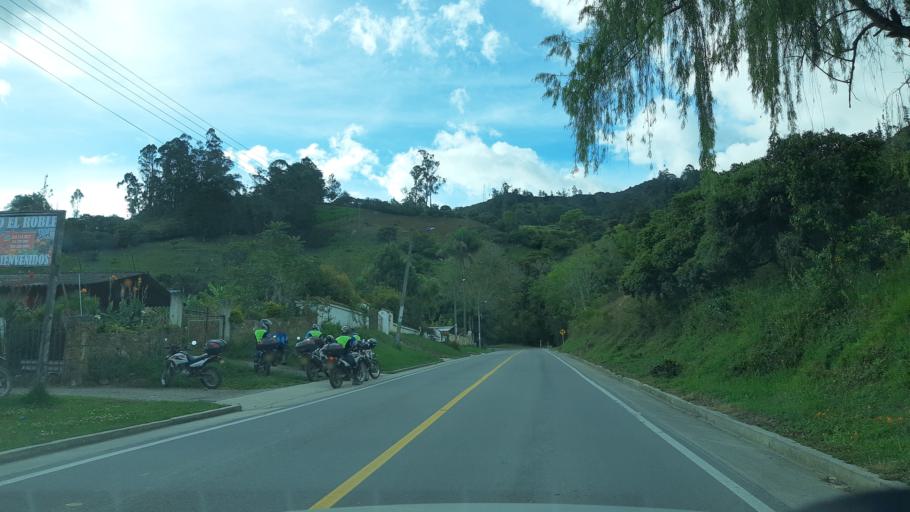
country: CO
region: Cundinamarca
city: Macheta
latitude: 5.0829
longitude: -73.6128
